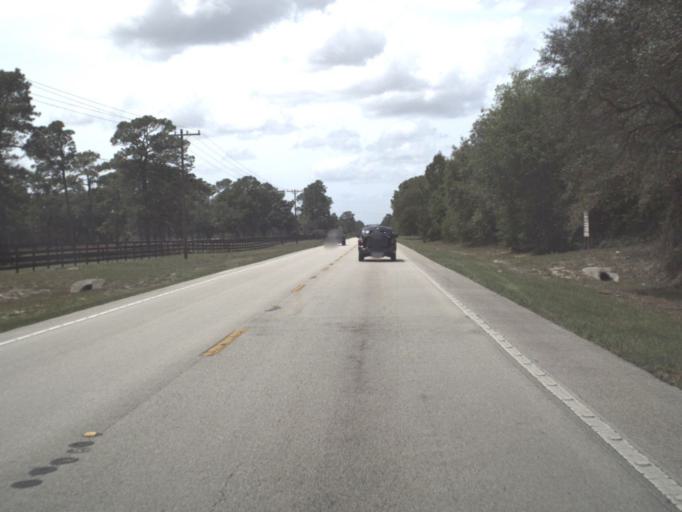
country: US
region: Florida
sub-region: Lake County
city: Mount Plymouth
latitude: 28.8667
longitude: -81.5026
